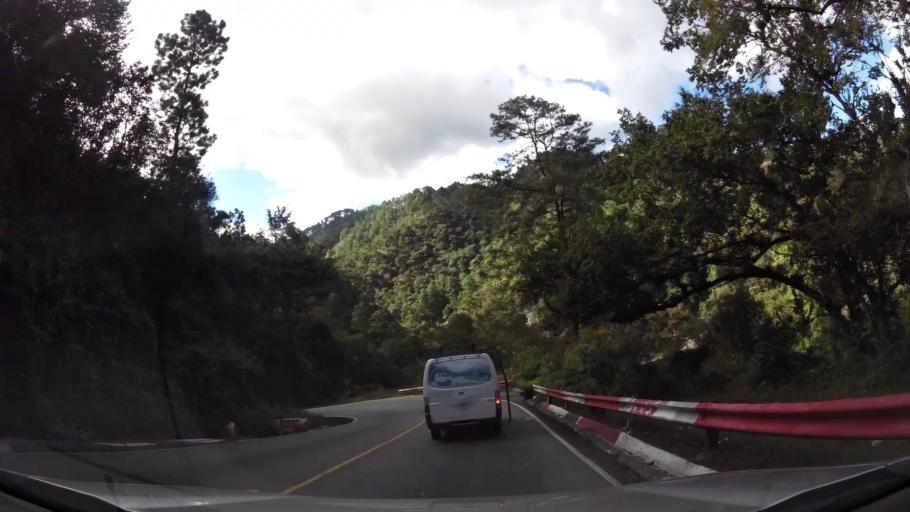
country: GT
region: Quiche
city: Chichicastenango
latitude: 14.9184
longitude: -91.1043
